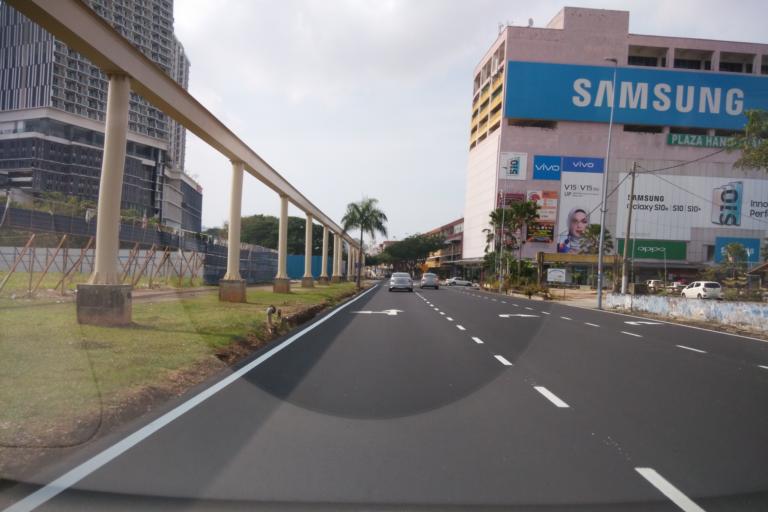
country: MY
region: Melaka
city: Malacca
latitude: 2.2041
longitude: 102.2483
